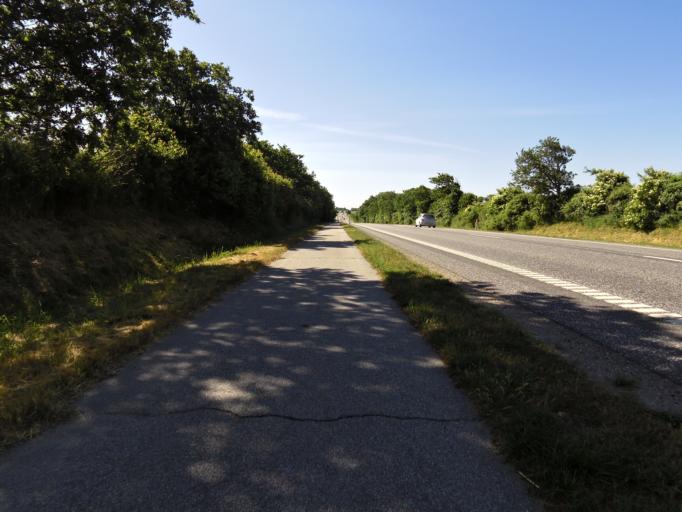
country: DK
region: Central Jutland
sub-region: Struer Kommune
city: Struer
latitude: 56.4622
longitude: 8.5895
